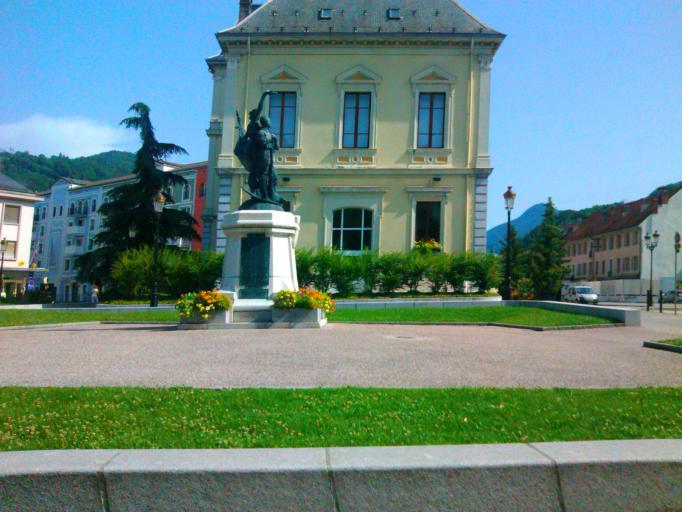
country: FR
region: Rhone-Alpes
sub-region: Departement de la Savoie
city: Albertville
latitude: 45.6751
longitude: 6.3926
